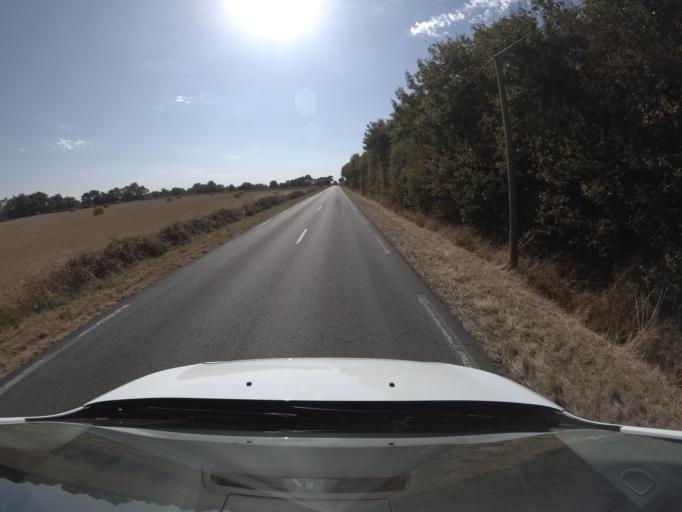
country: FR
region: Poitou-Charentes
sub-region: Departement des Deux-Sevres
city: Mauze-Thouarsais
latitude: 47.0033
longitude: -0.3589
